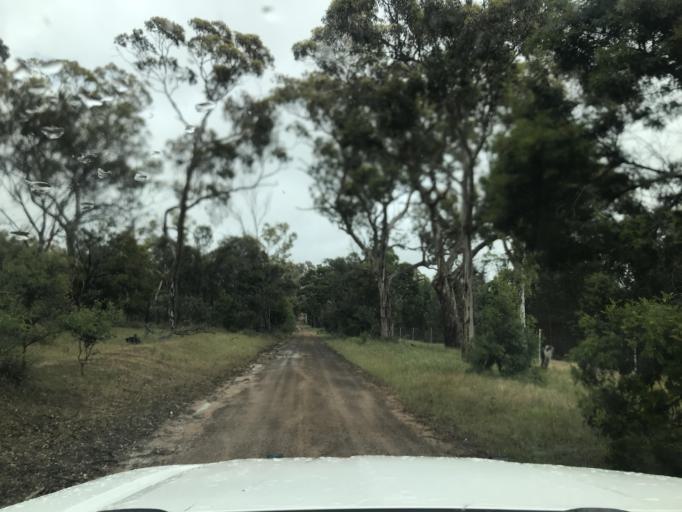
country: AU
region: South Australia
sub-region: Wattle Range
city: Penola
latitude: -37.2647
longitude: 141.3141
